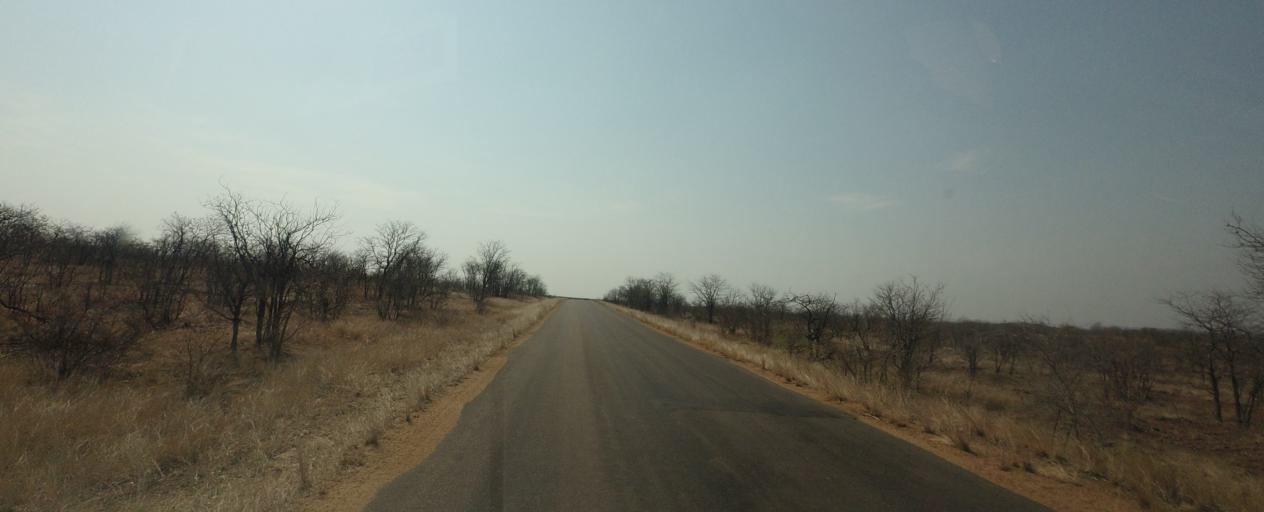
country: ZA
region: Limpopo
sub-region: Mopani District Municipality
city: Phalaborwa
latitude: -23.9499
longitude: 31.6179
